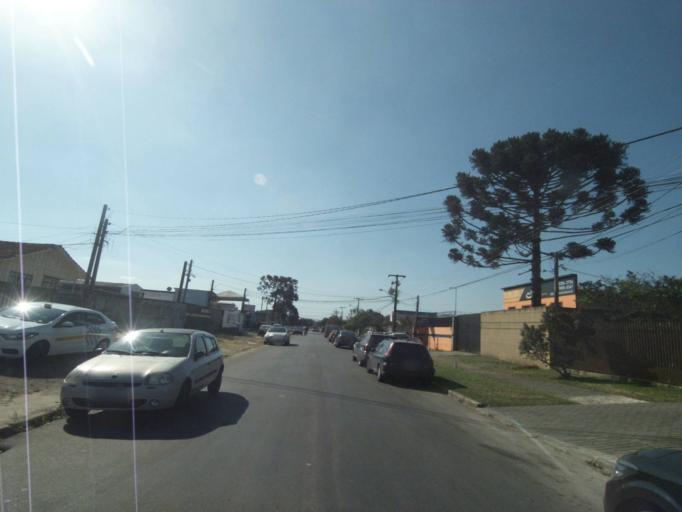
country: BR
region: Parana
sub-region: Sao Jose Dos Pinhais
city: Sao Jose dos Pinhais
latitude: -25.4871
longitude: -49.2363
